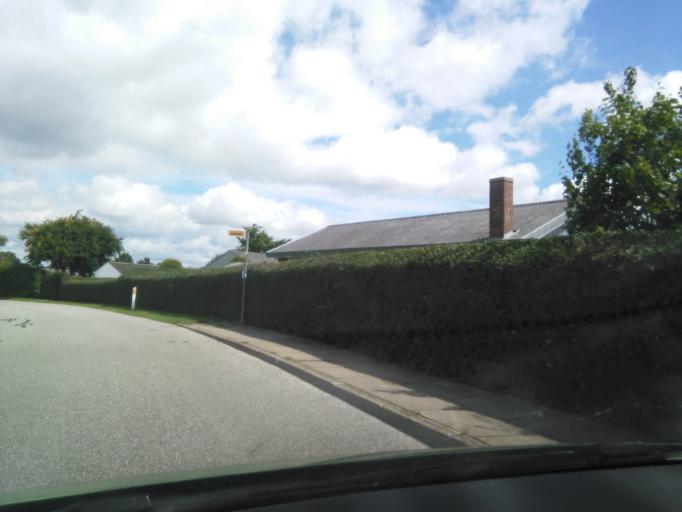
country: DK
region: Central Jutland
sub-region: Arhus Kommune
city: Logten
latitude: 56.2578
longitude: 10.3355
